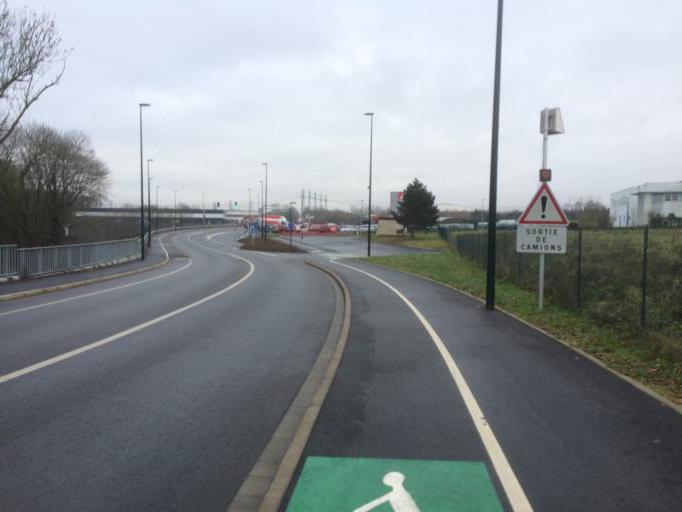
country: FR
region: Ile-de-France
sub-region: Departement de l'Essonne
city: Villejust
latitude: 48.6928
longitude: 2.2222
